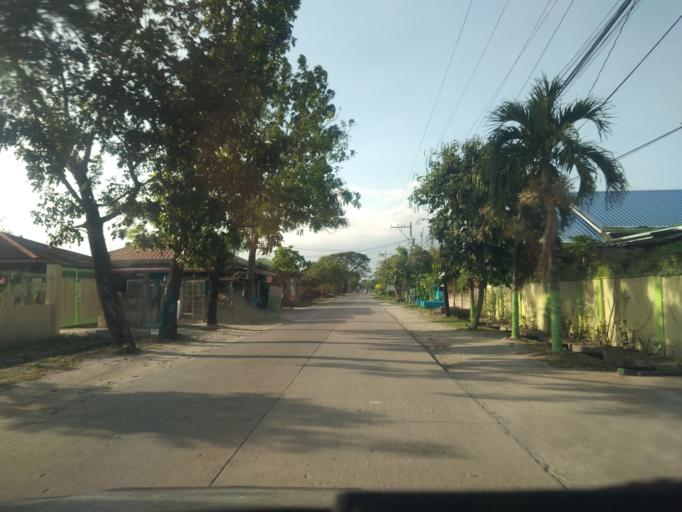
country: PH
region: Central Luzon
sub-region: Province of Pampanga
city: Bulaon
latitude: 15.0920
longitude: 120.6859
